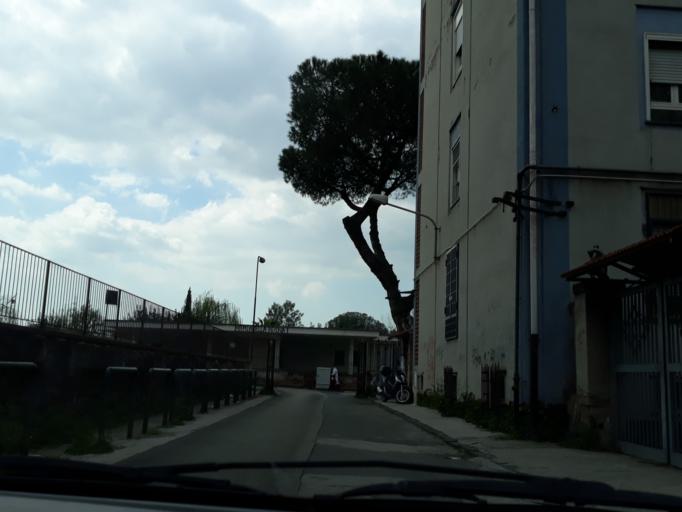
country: IT
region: Campania
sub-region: Provincia di Napoli
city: Melito di Napoli
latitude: 40.8918
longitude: 14.2320
